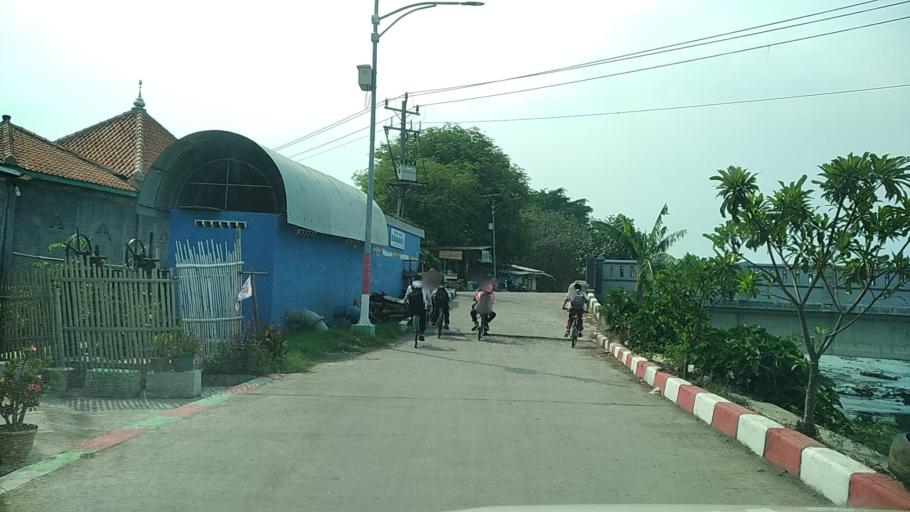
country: ID
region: Central Java
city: Semarang
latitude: -6.9594
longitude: 110.4147
